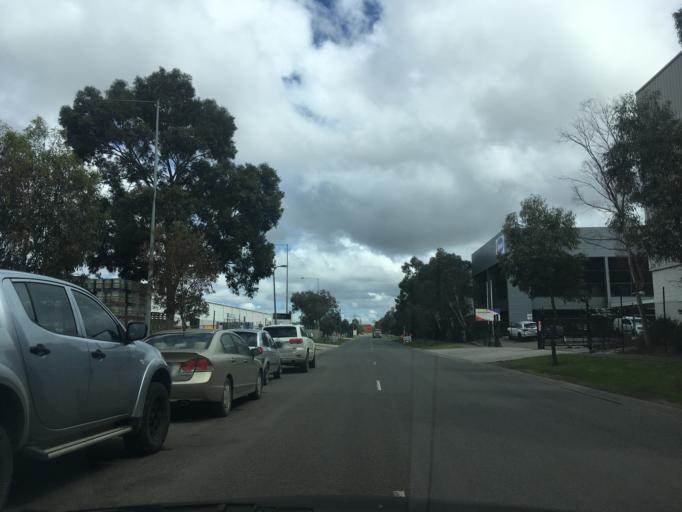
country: AU
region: Victoria
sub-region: Brimbank
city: Brooklyn
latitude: -37.8307
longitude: 144.8023
